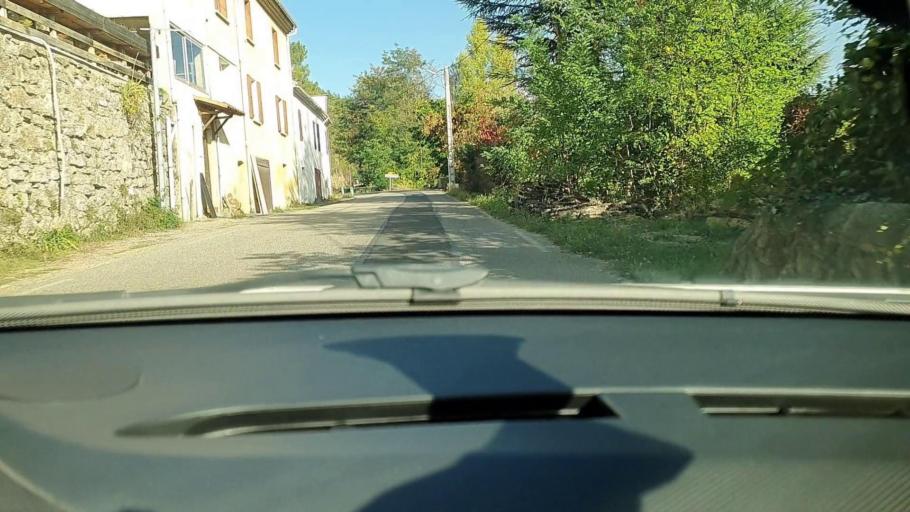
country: FR
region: Languedoc-Roussillon
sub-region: Departement du Gard
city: Besseges
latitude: 44.3051
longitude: 4.0934
